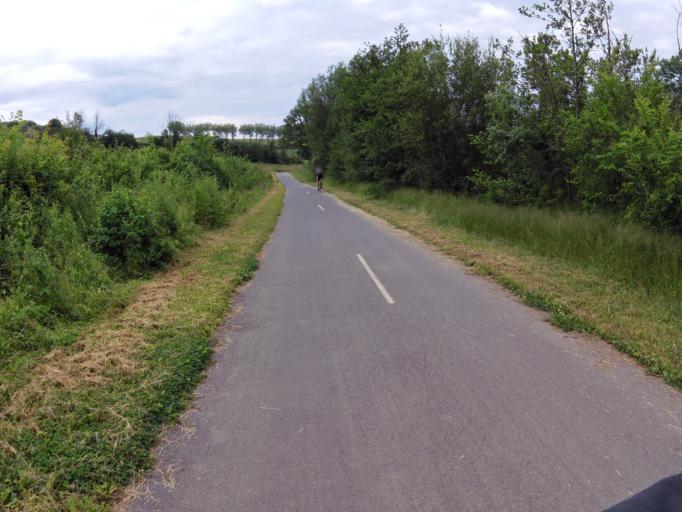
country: FR
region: Champagne-Ardenne
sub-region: Departement des Ardennes
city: Donchery
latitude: 49.6961
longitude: 4.8991
